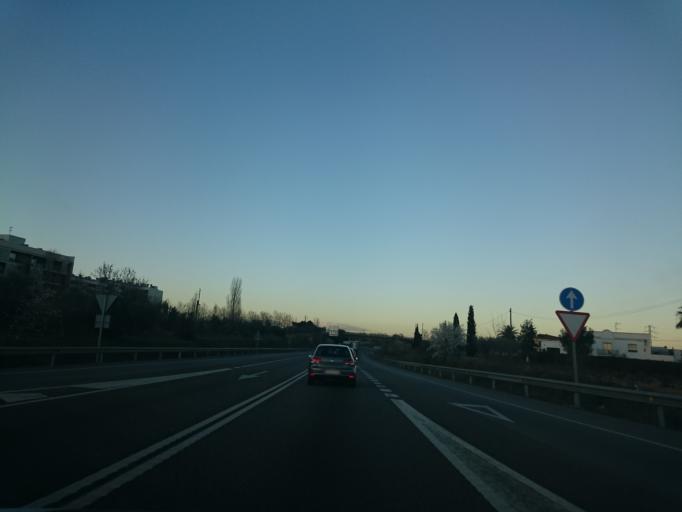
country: ES
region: Catalonia
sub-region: Provincia de Barcelona
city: Vilafranca del Penedes
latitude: 41.3377
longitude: 1.7075
